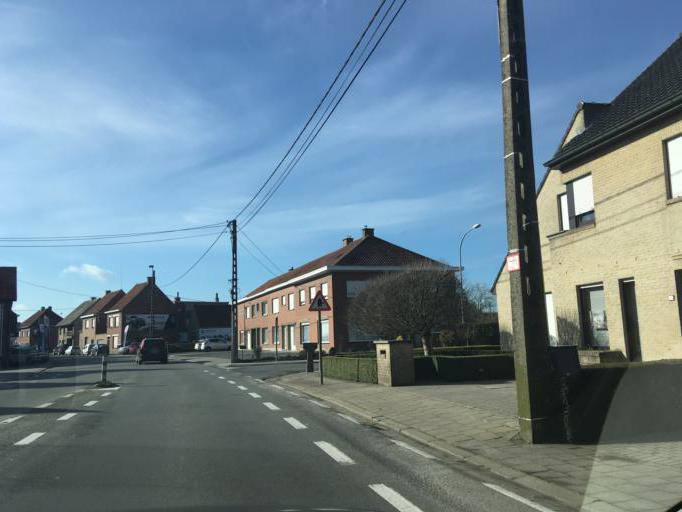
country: BE
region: Flanders
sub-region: Provincie West-Vlaanderen
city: Ledegem
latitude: 50.8715
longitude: 3.1475
